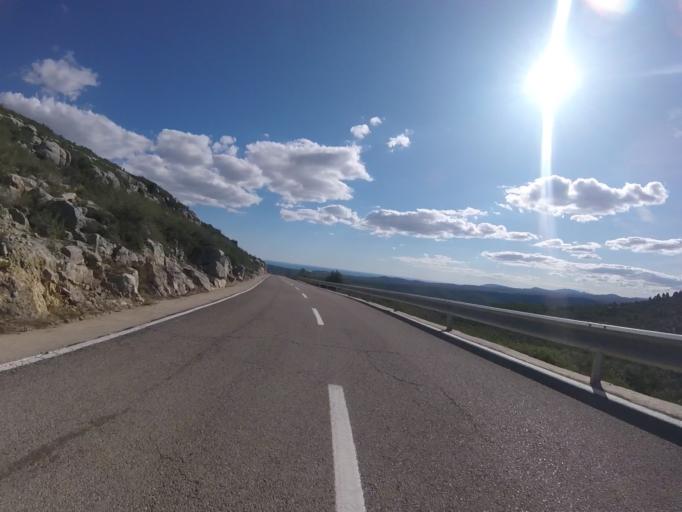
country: ES
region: Valencia
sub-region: Provincia de Castello
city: Alcala de Xivert
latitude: 40.2938
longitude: 0.1809
